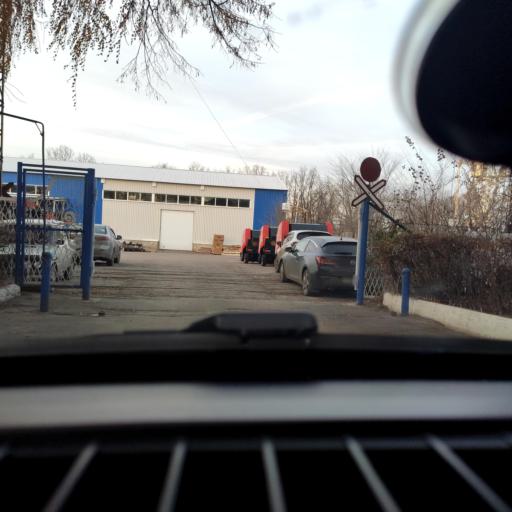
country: RU
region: Voronezj
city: Voronezh
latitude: 51.6670
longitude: 39.1412
